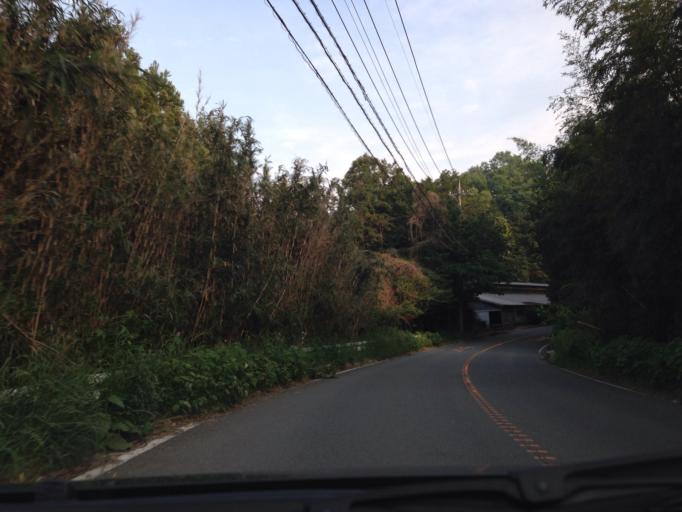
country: JP
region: Shizuoka
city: Mishima
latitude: 35.1617
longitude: 138.9339
